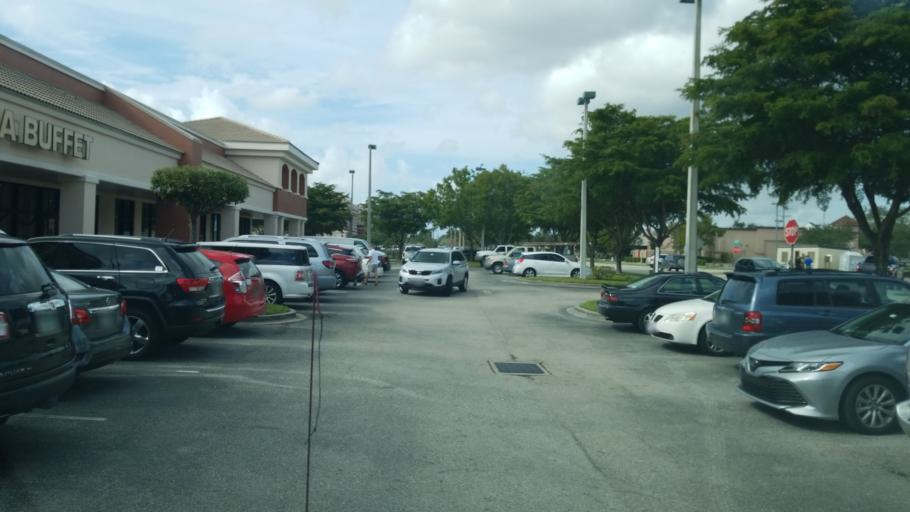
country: US
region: Florida
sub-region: Sarasota County
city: North Port
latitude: 27.0340
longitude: -82.2115
